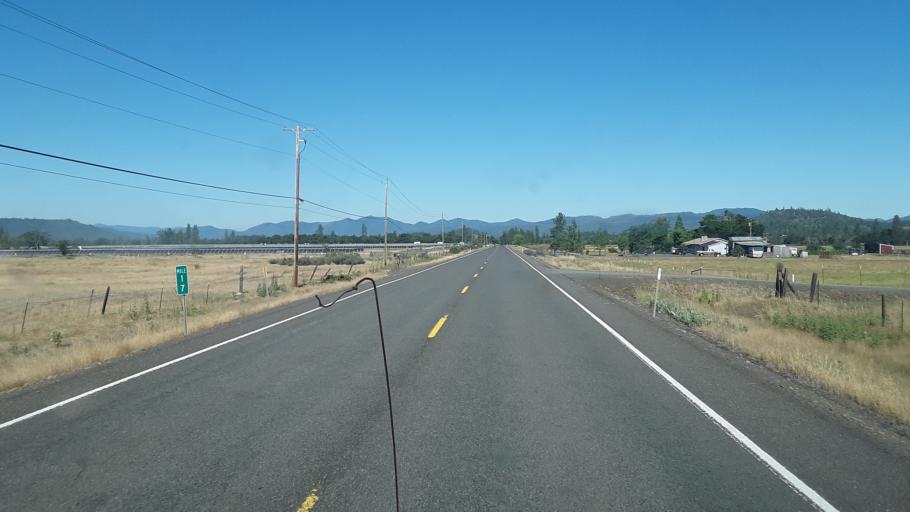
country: US
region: Oregon
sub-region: Jackson County
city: Eagle Point
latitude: 42.5237
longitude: -122.8232
